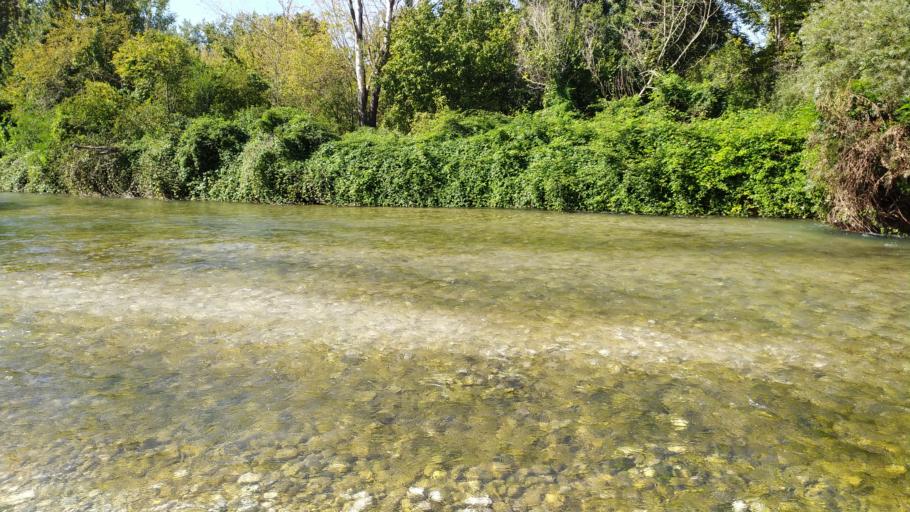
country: IT
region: Friuli Venezia Giulia
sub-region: Provincia di Pordenone
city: Cavolano-Schiavoi
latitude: 45.9389
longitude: 12.4873
